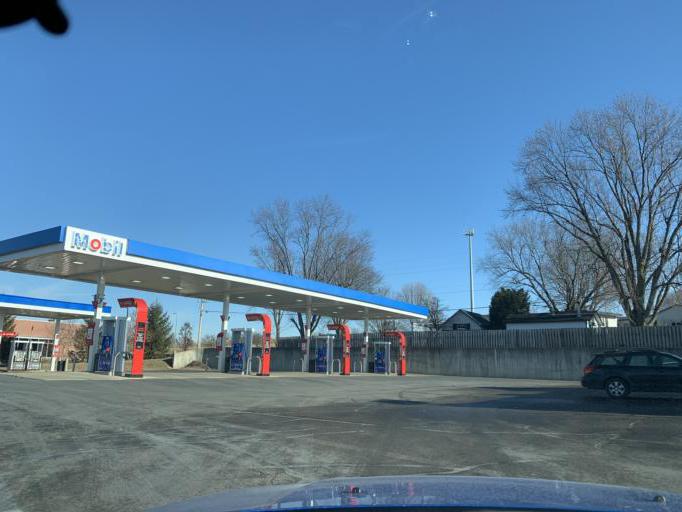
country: US
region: Wisconsin
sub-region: Green County
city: Monroe
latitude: 42.6146
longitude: -89.6365
